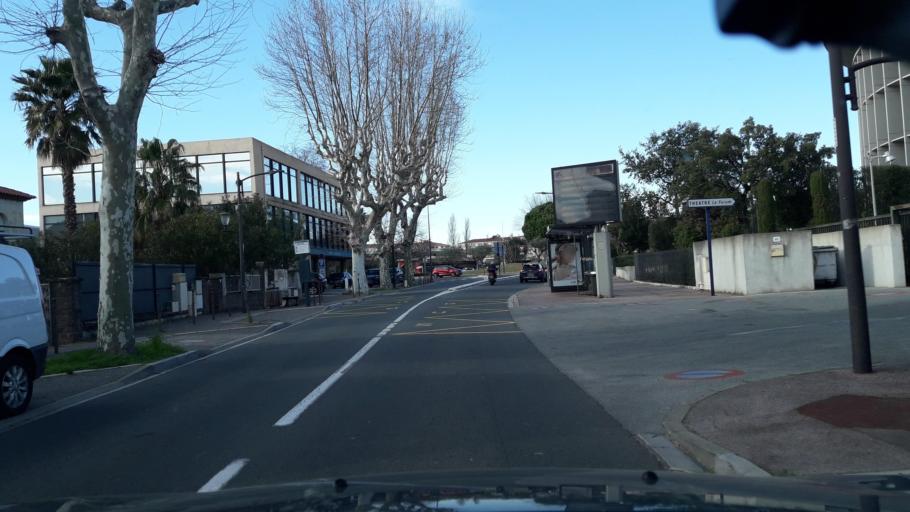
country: FR
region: Provence-Alpes-Cote d'Azur
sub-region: Departement du Var
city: Frejus
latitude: 43.4269
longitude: 6.7373
